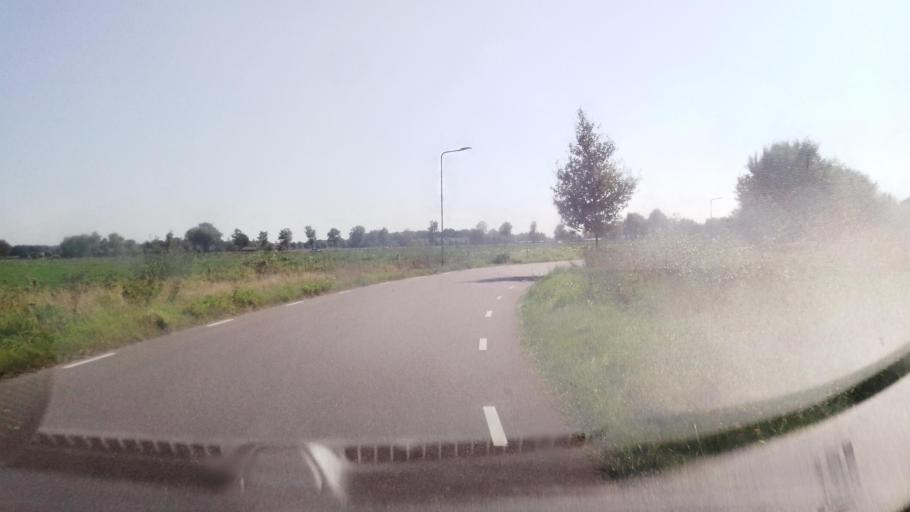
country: NL
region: Limburg
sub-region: Gemeente Peel en Maas
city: Maasbree
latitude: 51.4211
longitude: 5.9846
